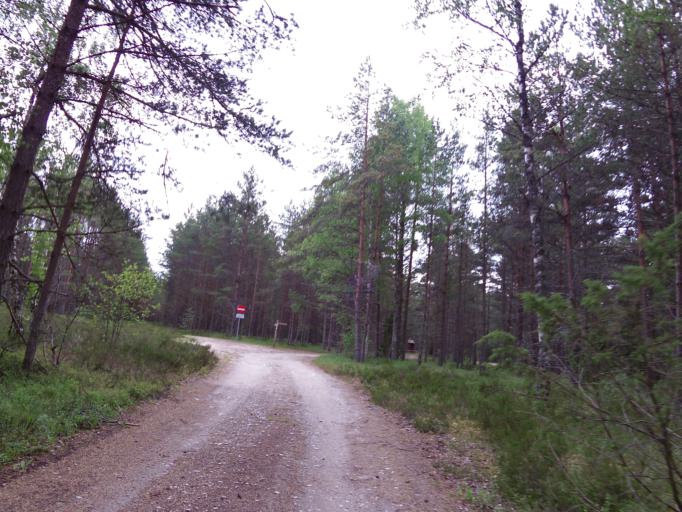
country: EE
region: Harju
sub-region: Paldiski linn
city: Paldiski
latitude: 59.2450
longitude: 23.7473
